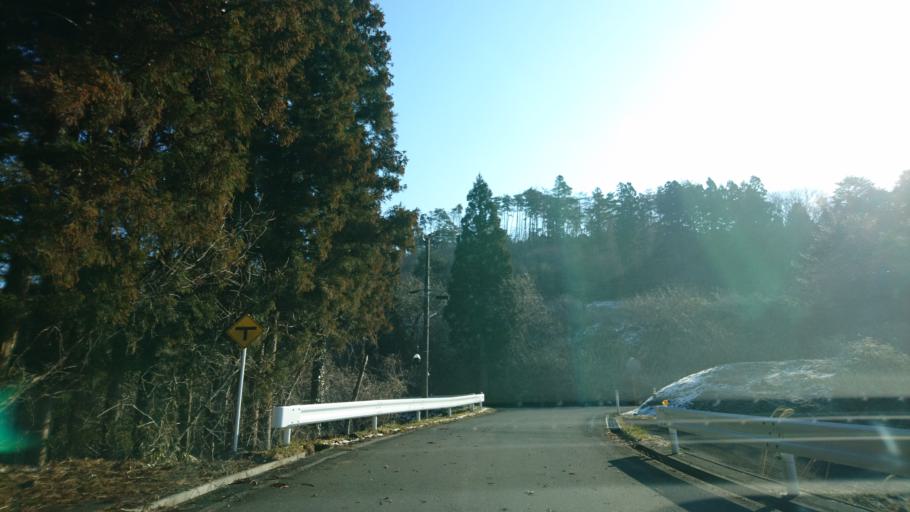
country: JP
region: Iwate
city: Ichinoseki
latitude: 38.9185
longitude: 141.2867
